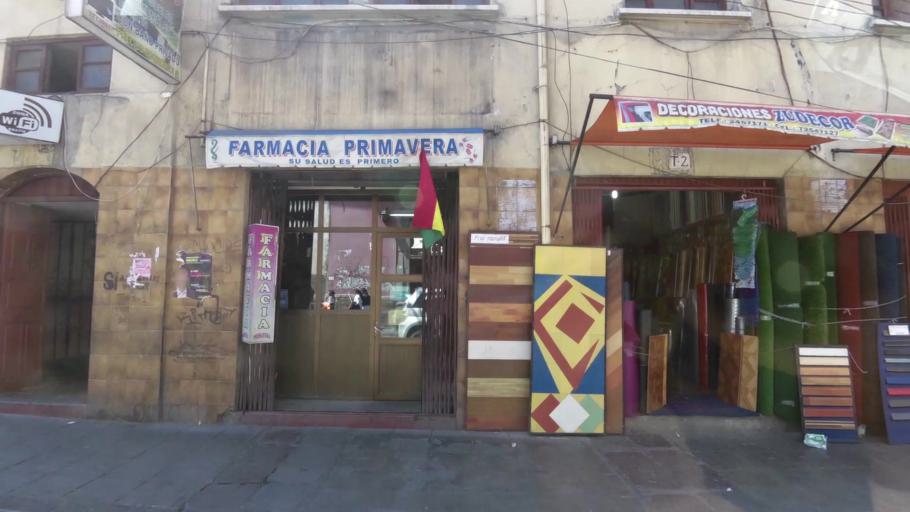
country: BO
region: La Paz
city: La Paz
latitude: -16.4931
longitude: -68.1407
